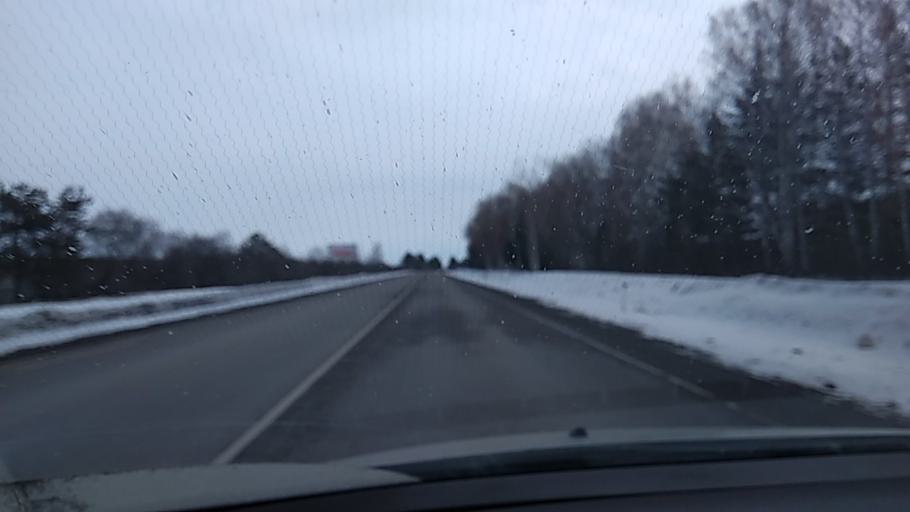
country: RU
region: Sverdlovsk
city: Dvurechensk
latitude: 56.6751
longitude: 61.1377
